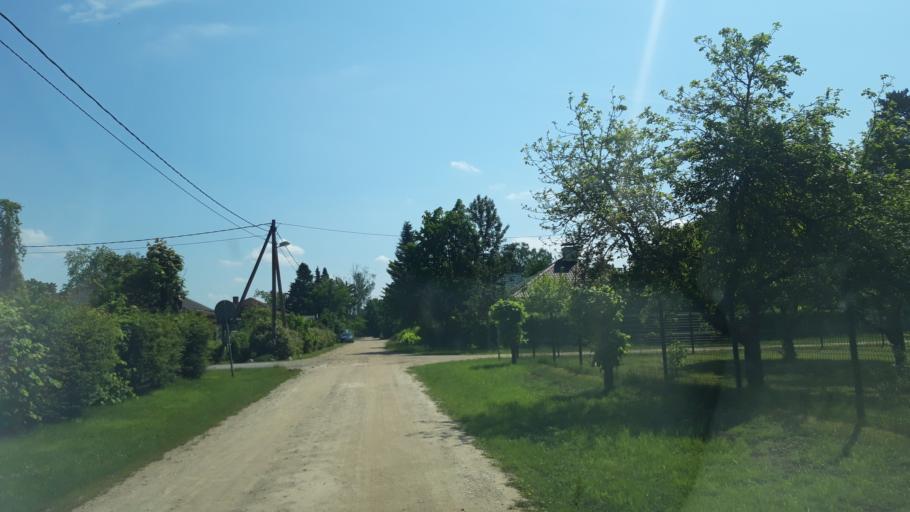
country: LV
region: Saulkrastu
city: Saulkrasti
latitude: 57.2570
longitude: 24.4112
